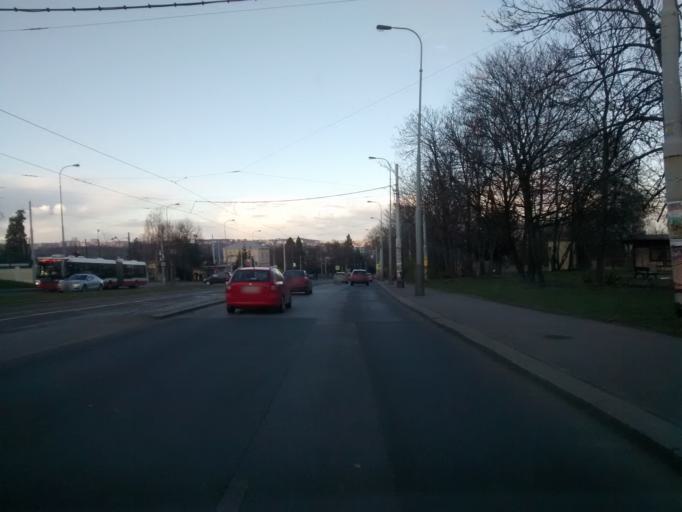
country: CZ
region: Praha
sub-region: Praha 1
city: Mala Strana
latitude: 50.0930
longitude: 14.3883
